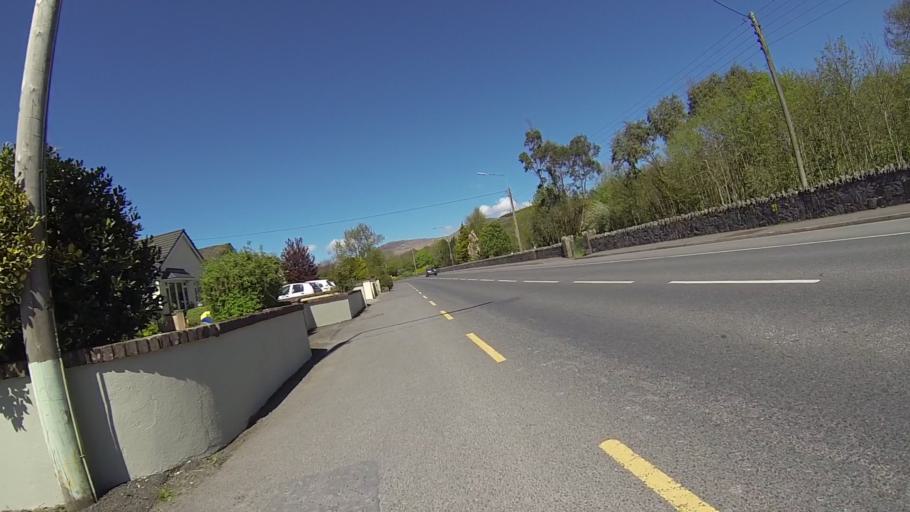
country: IE
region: Munster
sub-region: Ciarrai
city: Kenmare
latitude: 51.8823
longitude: -9.5852
